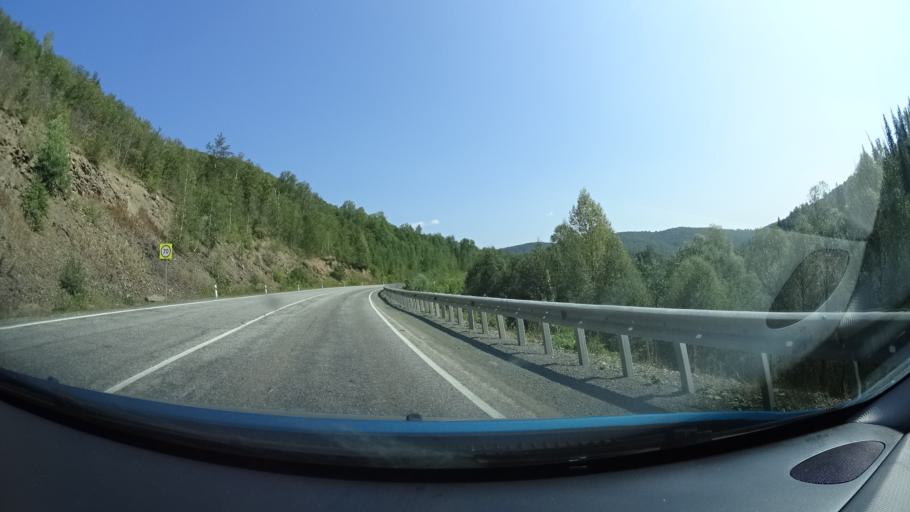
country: RU
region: Bashkortostan
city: Inzer
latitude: 54.3382
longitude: 57.1463
